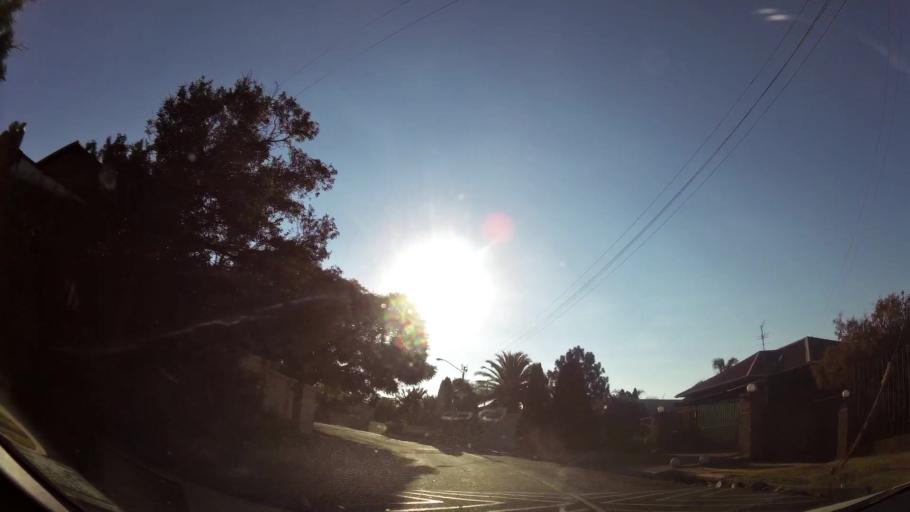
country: ZA
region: Gauteng
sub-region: Ekurhuleni Metropolitan Municipality
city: Germiston
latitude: -26.1893
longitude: 28.1489
